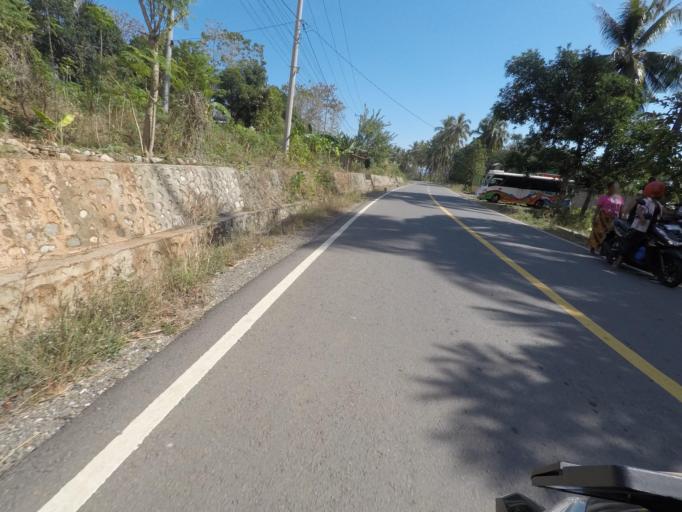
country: TL
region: Bobonaro
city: Maliana
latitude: -8.9527
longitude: 125.2109
